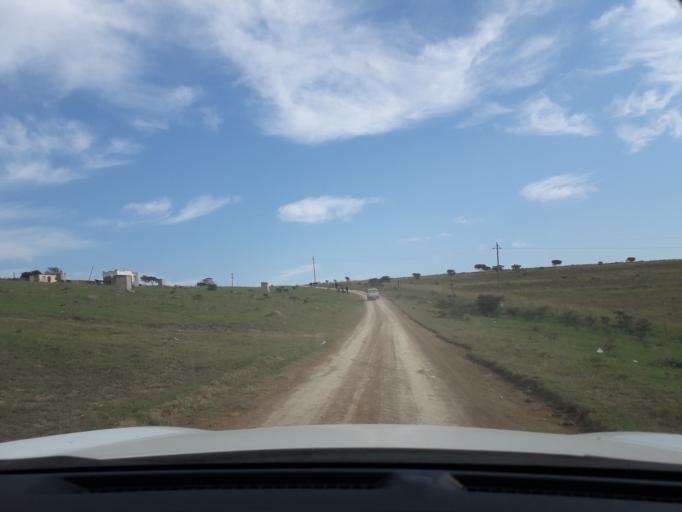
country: ZA
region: Eastern Cape
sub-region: Buffalo City Metropolitan Municipality
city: Bhisho
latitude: -32.9975
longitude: 27.3333
